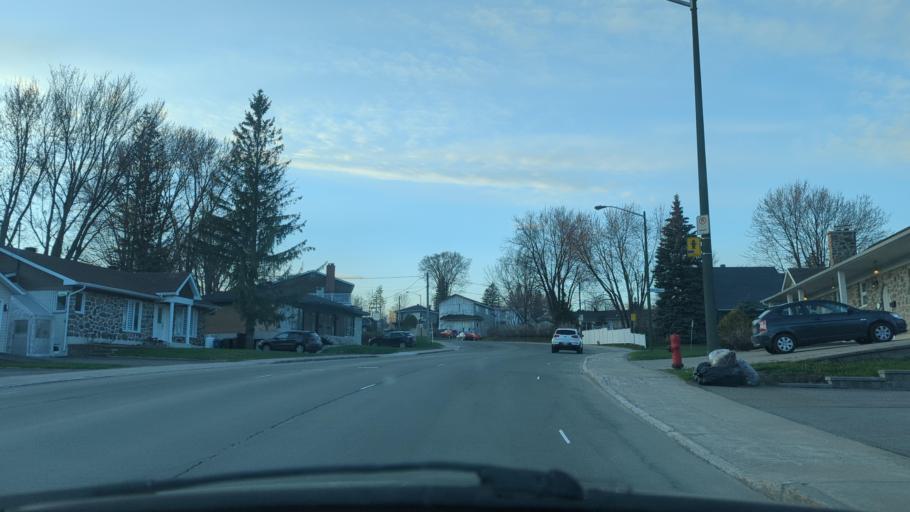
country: CA
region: Quebec
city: Quebec
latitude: 46.8509
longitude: -71.2624
